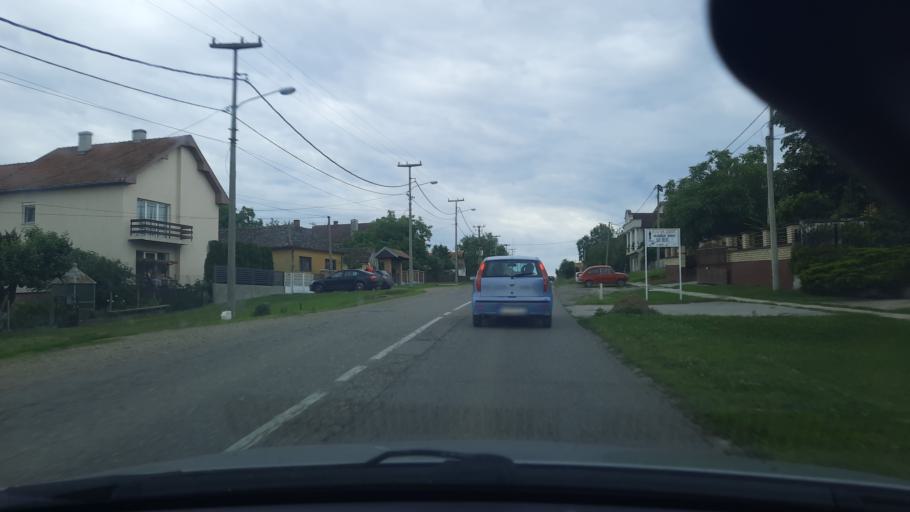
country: RS
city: Jevremovac
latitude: 44.7297
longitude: 19.6697
